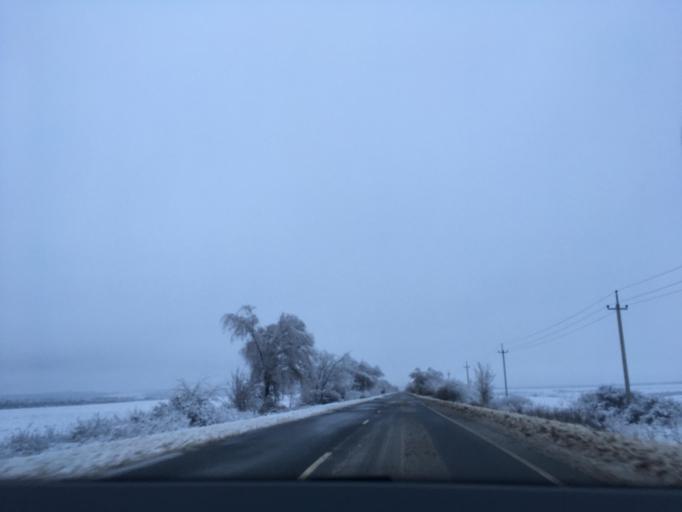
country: RU
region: Voronezj
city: Verkhniy Mamon
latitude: 50.0218
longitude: 40.0948
